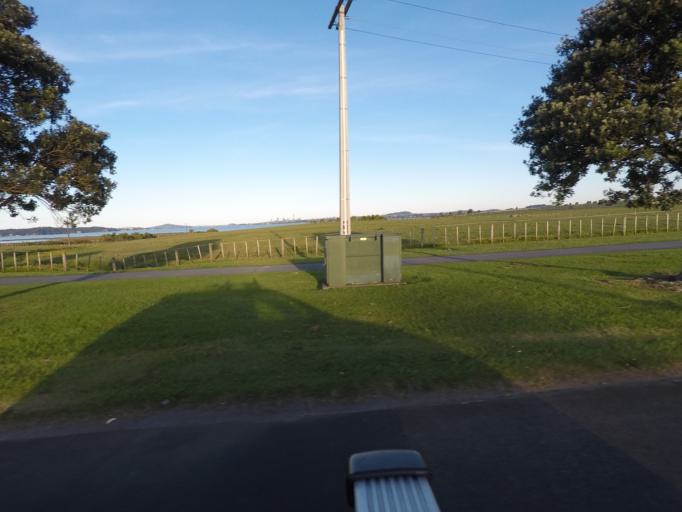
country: NZ
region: Auckland
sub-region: Auckland
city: Rosebank
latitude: -36.8522
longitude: 174.6511
